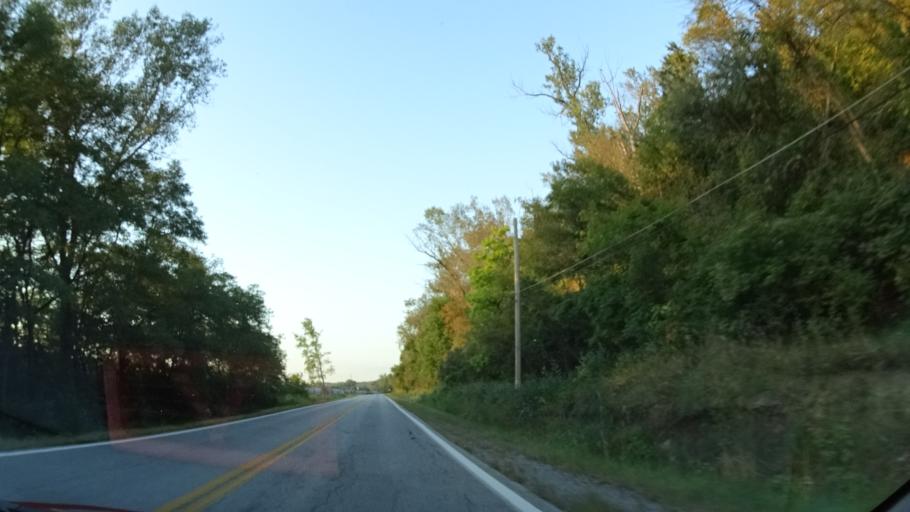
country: US
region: Iowa
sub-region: Pottawattamie County
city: Council Bluffs
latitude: 41.2795
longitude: -95.8602
